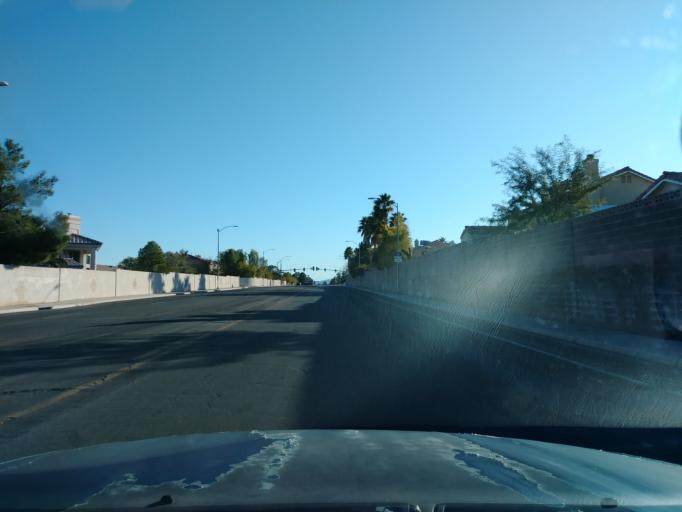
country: US
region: Nevada
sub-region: Clark County
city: Spring Valley
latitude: 36.1535
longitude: -115.2709
